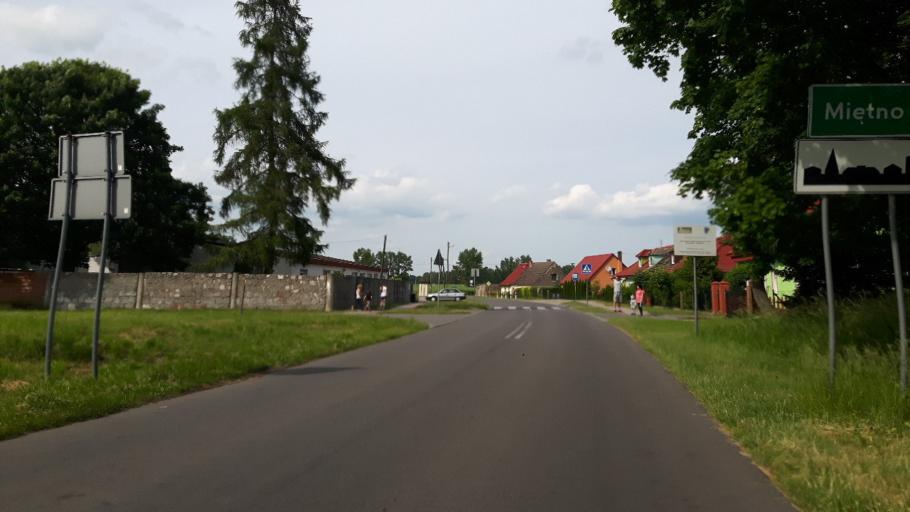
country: PL
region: West Pomeranian Voivodeship
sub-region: Powiat goleniowski
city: Nowogard
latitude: 53.7099
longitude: 15.1187
